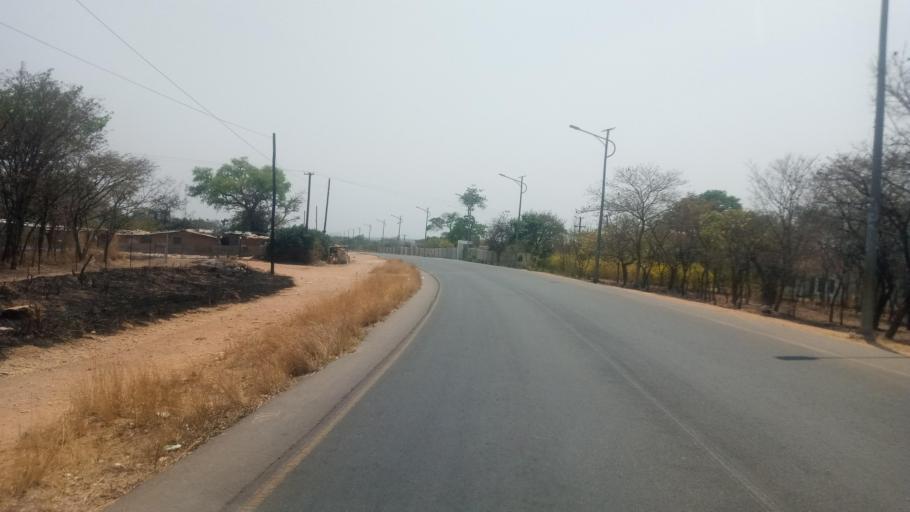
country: ZM
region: Lusaka
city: Lusaka
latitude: -15.4666
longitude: 28.4313
